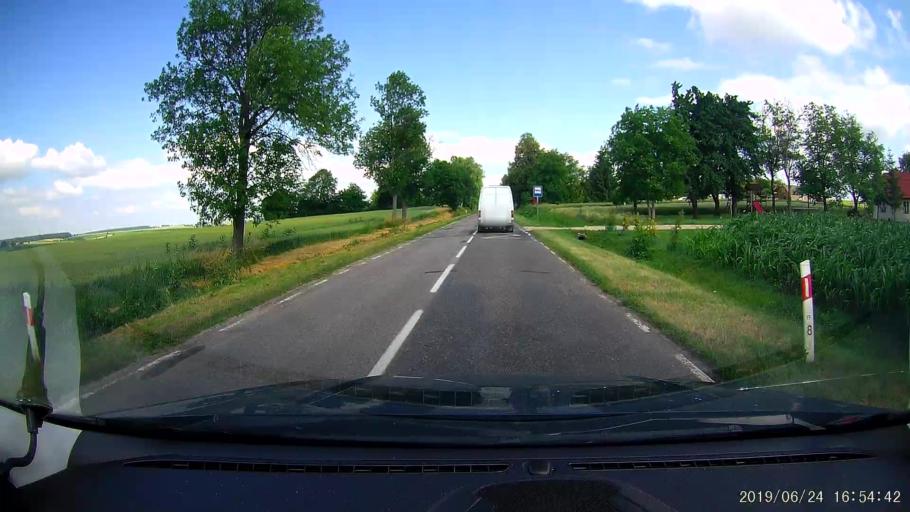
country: PL
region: Lublin Voivodeship
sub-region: Powiat tomaszowski
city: Telatyn
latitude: 50.5309
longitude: 23.8189
